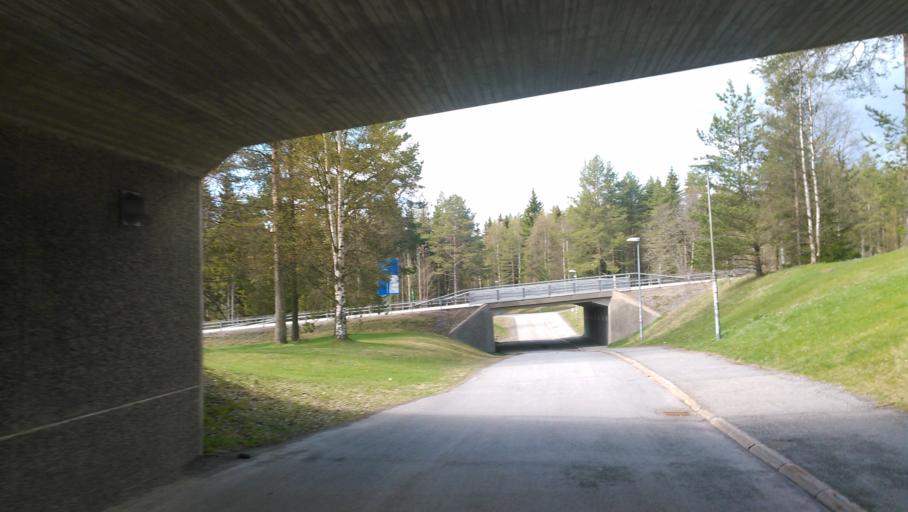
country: SE
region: Vaesterbotten
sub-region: Umea Kommun
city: Umea
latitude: 63.8038
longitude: 20.3181
